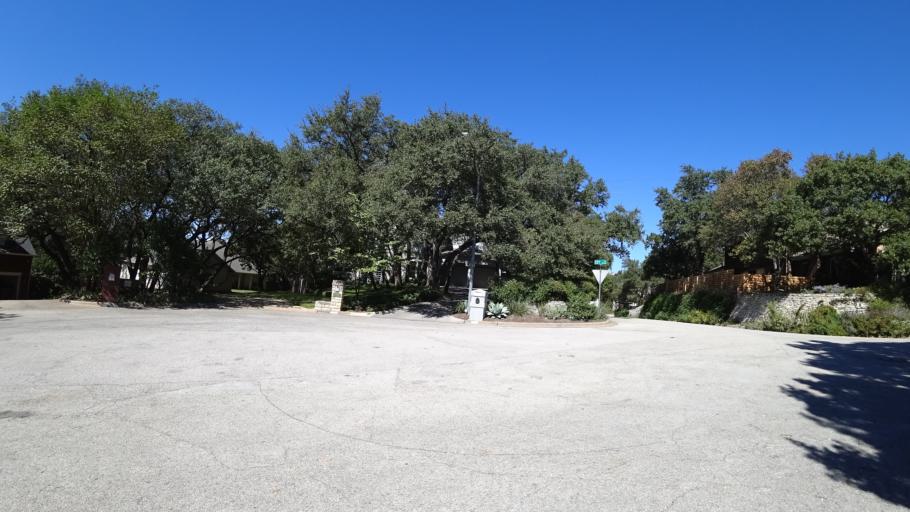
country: US
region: Texas
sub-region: Travis County
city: West Lake Hills
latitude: 30.3381
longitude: -97.7811
